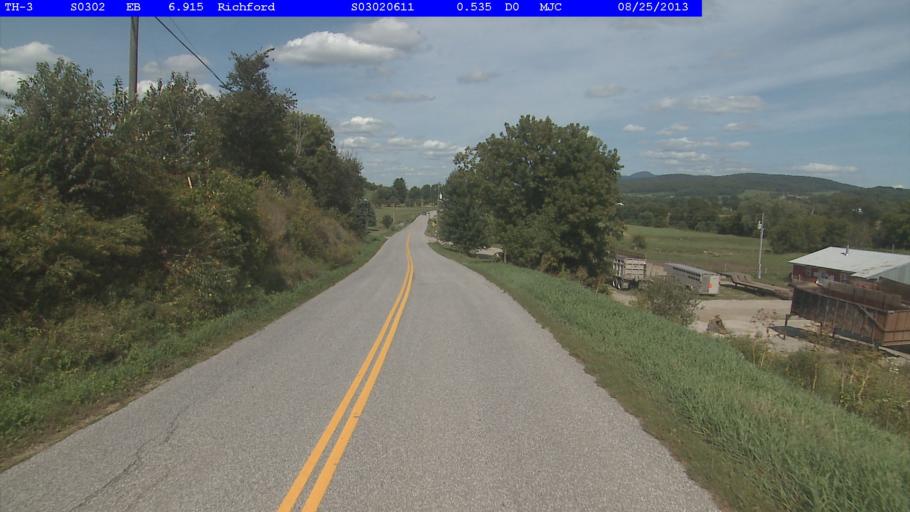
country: US
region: Vermont
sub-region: Franklin County
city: Richford
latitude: 44.9938
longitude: -72.6861
